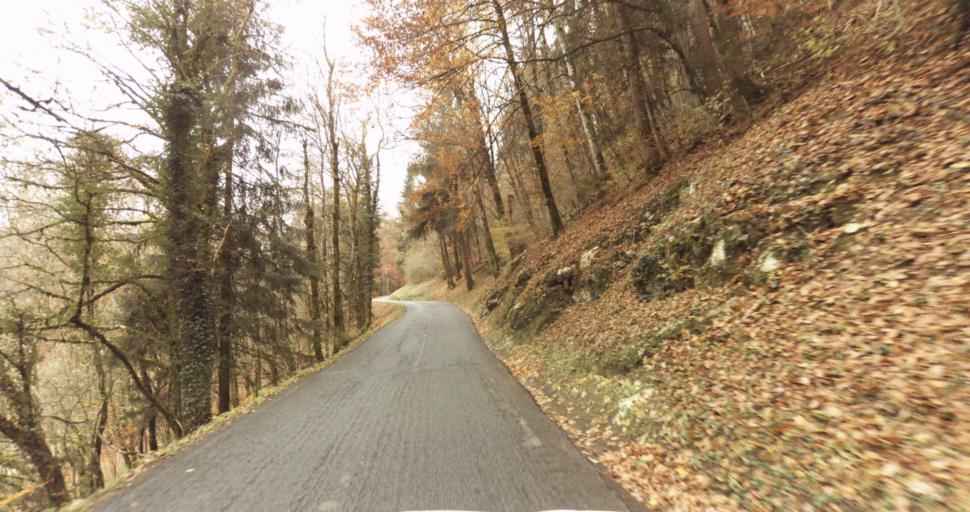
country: FR
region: Rhone-Alpes
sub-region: Departement de la Haute-Savoie
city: Gruffy
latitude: 45.7410
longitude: 6.0951
